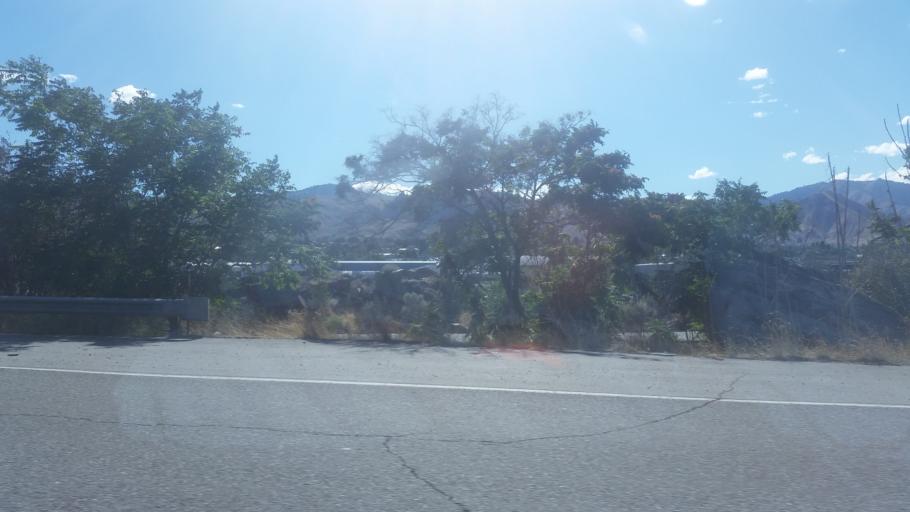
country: US
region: Washington
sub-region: Douglas County
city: East Wenatchee
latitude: 47.4138
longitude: -120.2943
